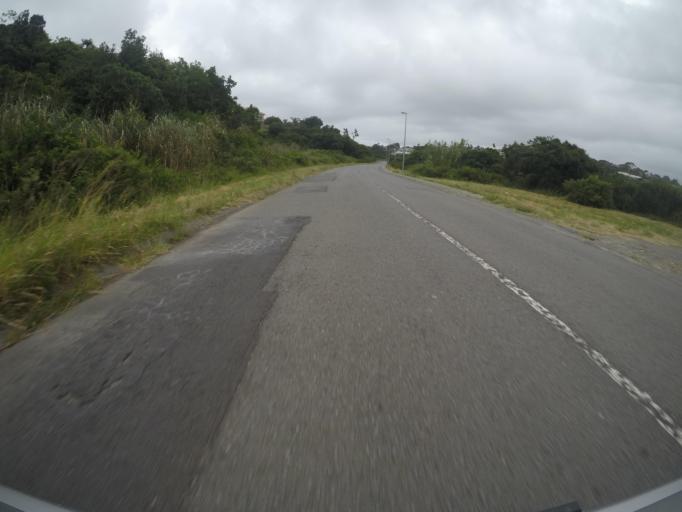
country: ZA
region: Eastern Cape
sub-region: Buffalo City Metropolitan Municipality
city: East London
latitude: -32.9785
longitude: 27.9333
